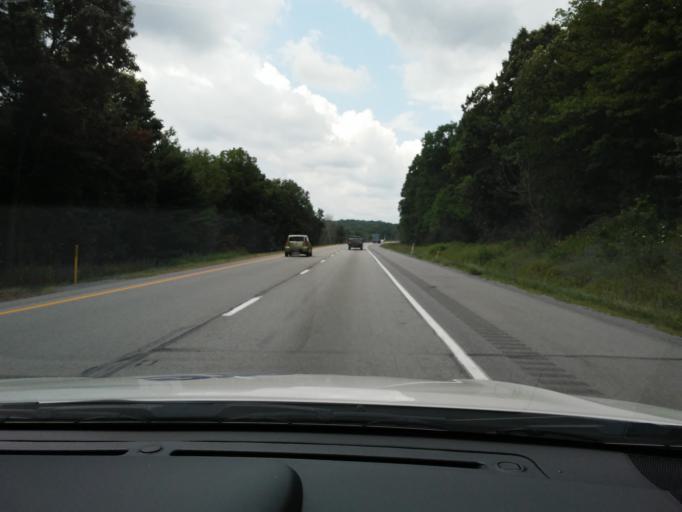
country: US
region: Pennsylvania
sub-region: Clearfield County
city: Troy
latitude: 40.9867
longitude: -78.1801
